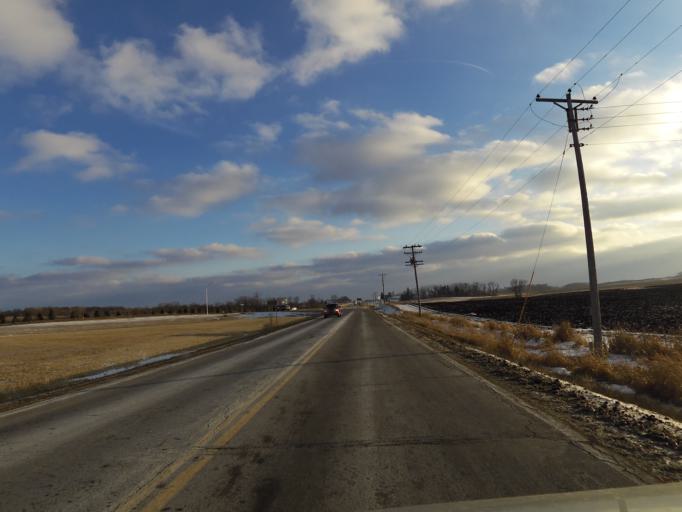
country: US
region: Minnesota
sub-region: Scott County
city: Prior Lake
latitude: 44.6886
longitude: -93.5009
